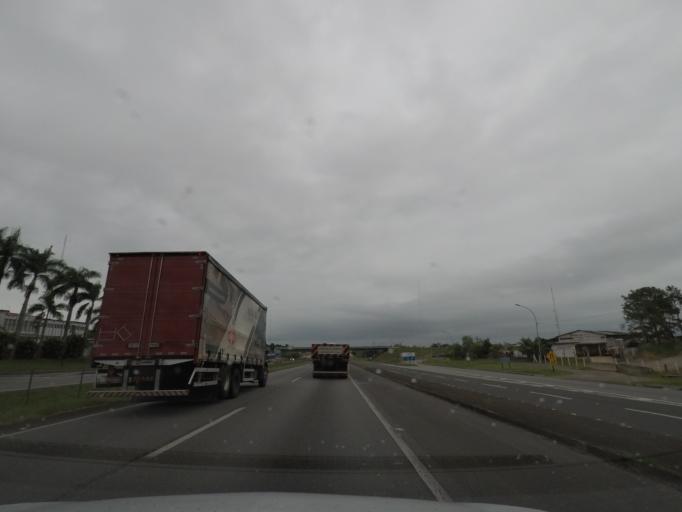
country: BR
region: Sao Paulo
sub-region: Registro
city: Registro
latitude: -24.5061
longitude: -47.8484
